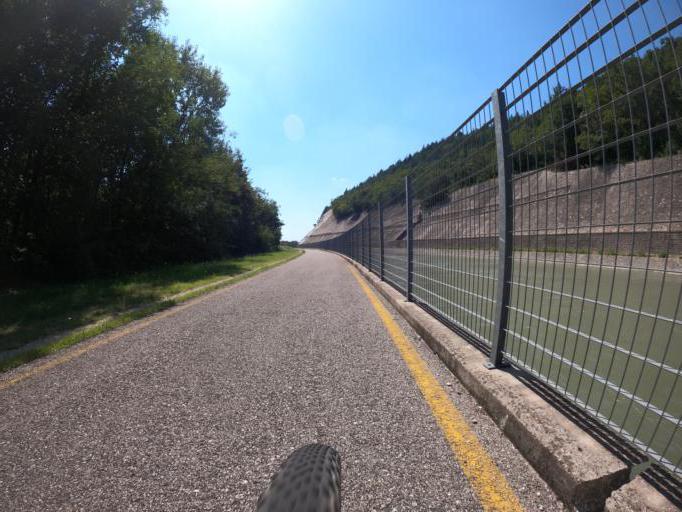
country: IT
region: Veneto
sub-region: Provincia di Verona
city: Volargne
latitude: 45.5514
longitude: 10.8199
